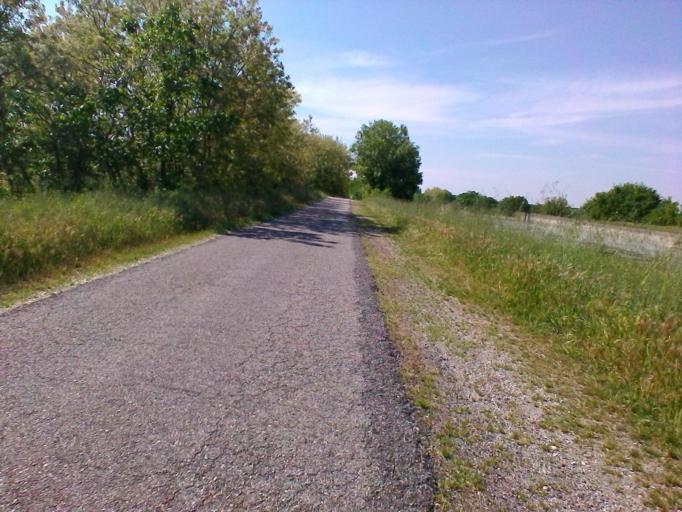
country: IT
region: Lombardy
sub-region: Provincia di Mantova
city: Soave
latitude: 45.2110
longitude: 10.7129
